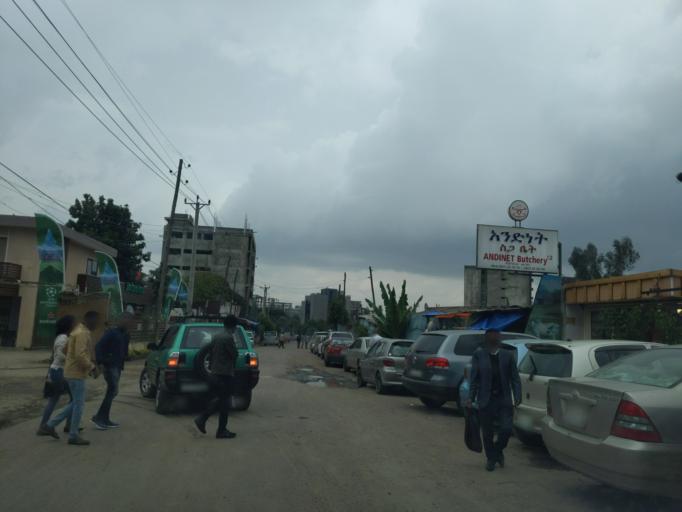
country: ET
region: Adis Abeba
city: Addis Ababa
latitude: 8.9973
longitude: 38.7696
